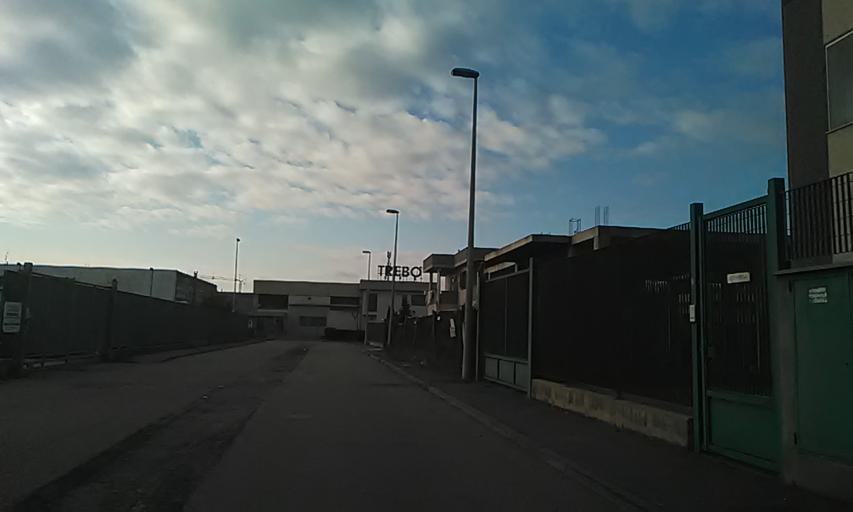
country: IT
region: Piedmont
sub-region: Provincia di Vercelli
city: Vercelli
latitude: 45.3197
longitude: 8.3969
